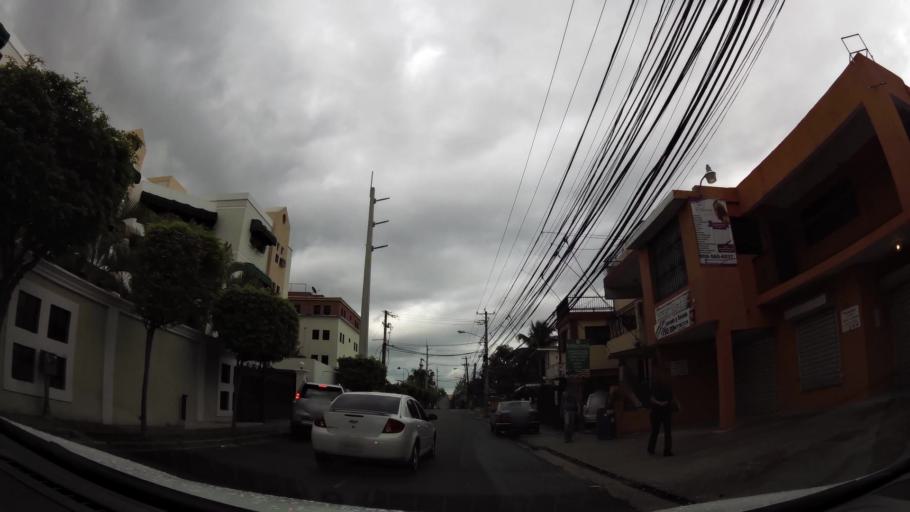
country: DO
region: Nacional
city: La Agustina
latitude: 18.4870
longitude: -69.9346
